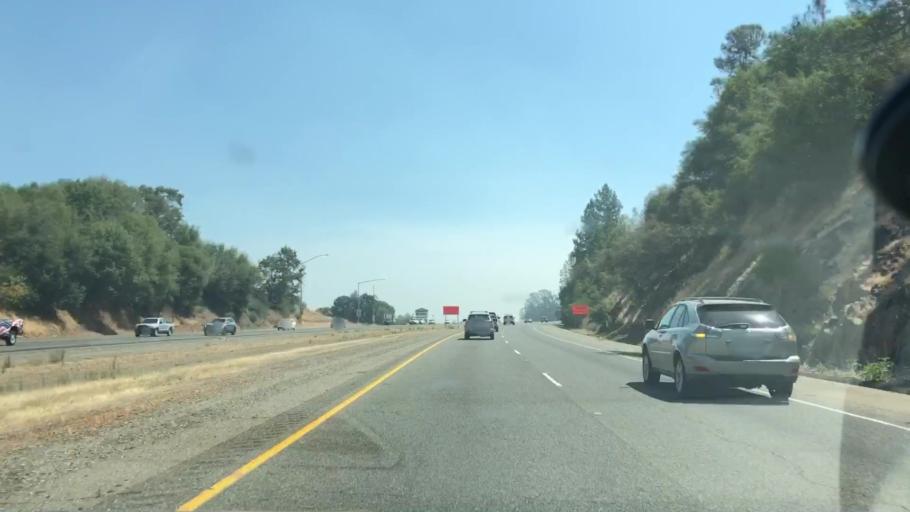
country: US
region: California
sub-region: El Dorado County
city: Diamond Springs
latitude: 38.7077
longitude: -120.8476
